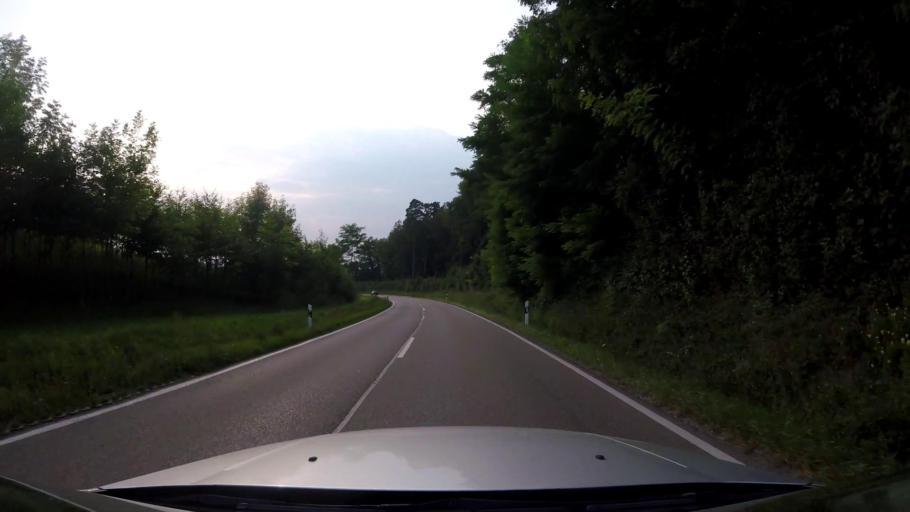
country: DE
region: Baden-Wuerttemberg
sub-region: Regierungsbezirk Stuttgart
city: Urbach
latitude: 48.8580
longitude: 9.5881
